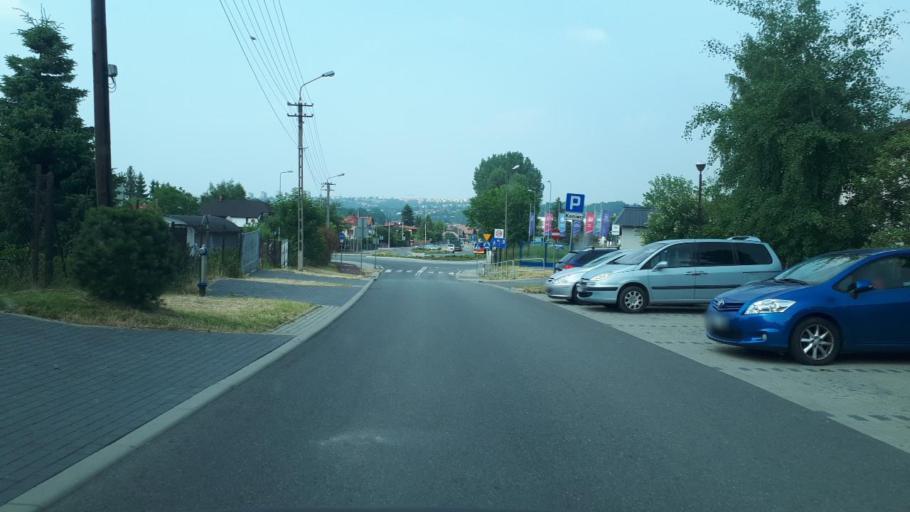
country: PL
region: Silesian Voivodeship
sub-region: Powiat bielski
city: Bystra
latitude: 49.7830
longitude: 19.0552
